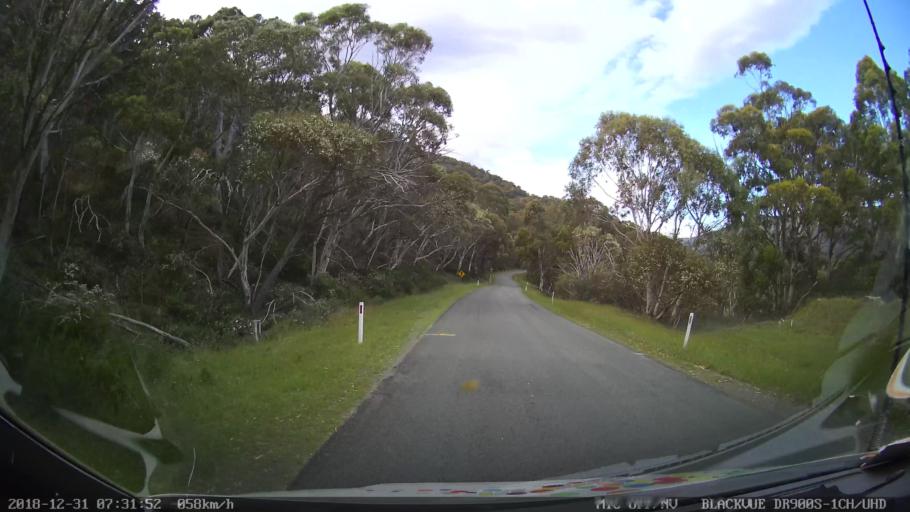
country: AU
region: New South Wales
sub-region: Snowy River
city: Jindabyne
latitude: -36.3282
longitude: 148.4697
